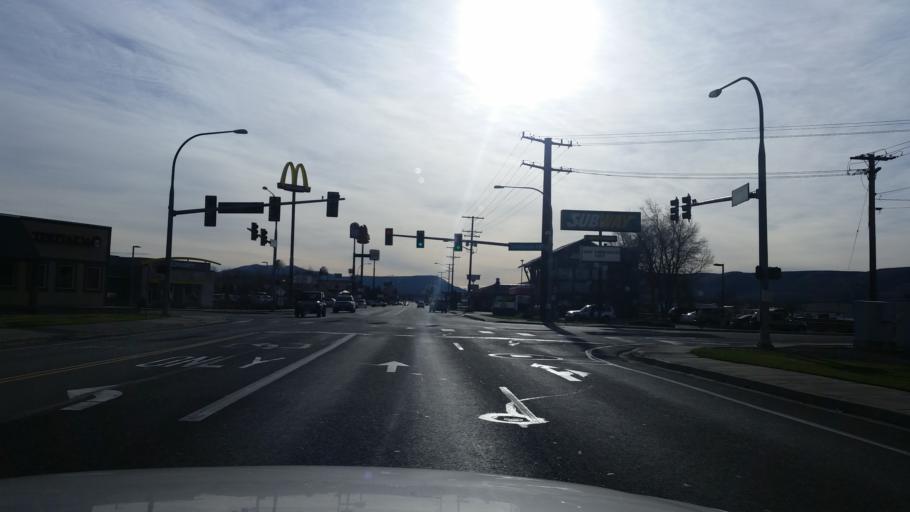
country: US
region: Washington
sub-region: Kittitas County
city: Ellensburg
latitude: 46.9812
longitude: -120.5458
